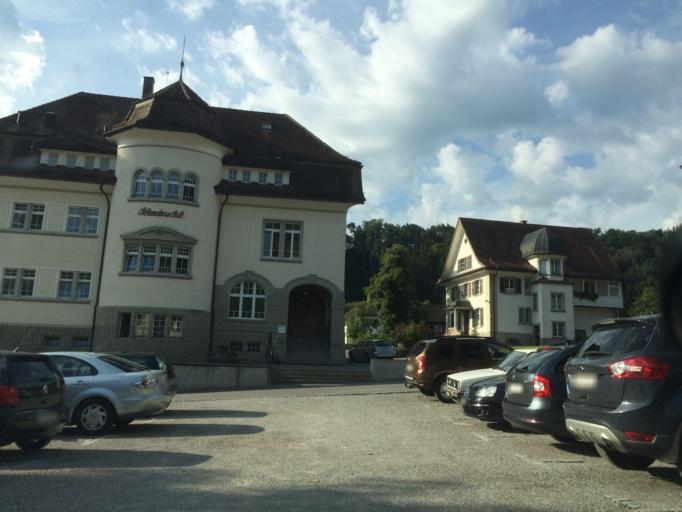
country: CH
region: Appenzell Innerrhoden
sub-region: Appenzell Inner Rhodes
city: Balgach
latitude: 47.4246
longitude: 9.6102
